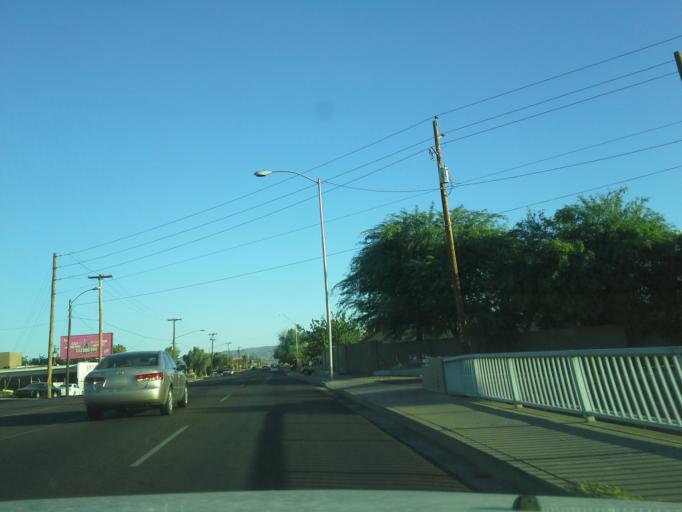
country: US
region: Arizona
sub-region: Maricopa County
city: Phoenix
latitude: 33.4774
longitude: -112.0303
